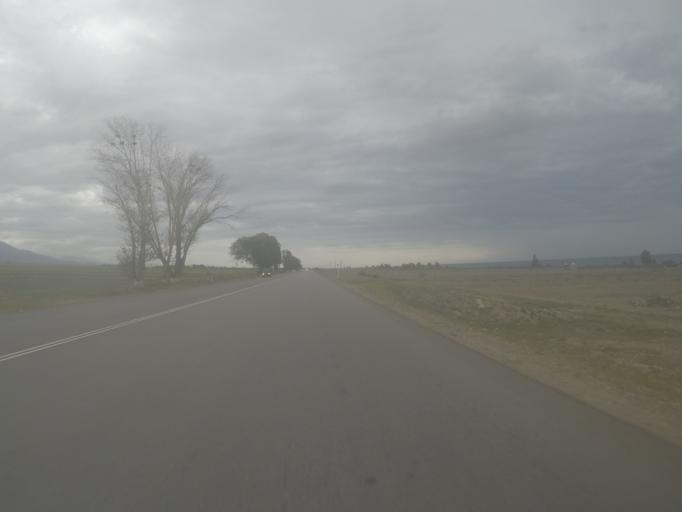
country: KG
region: Ysyk-Koel
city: Cholpon-Ata
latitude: 42.5984
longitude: 76.7983
